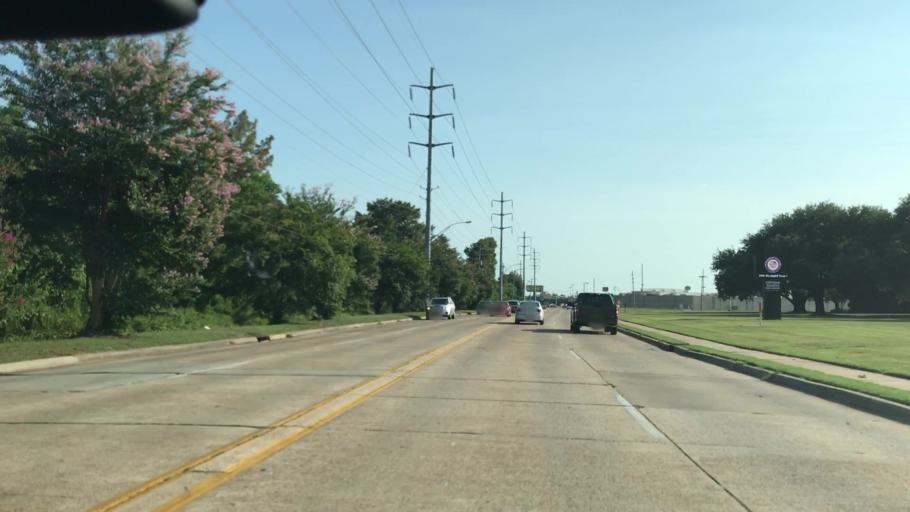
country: US
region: Louisiana
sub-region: Bossier Parish
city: Bossier City
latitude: 32.4486
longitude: -93.7108
